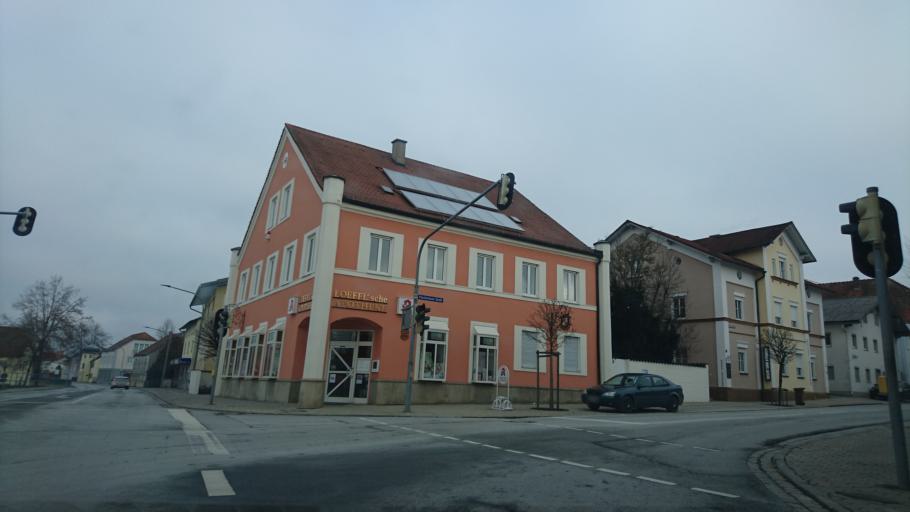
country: DE
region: Bavaria
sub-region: Lower Bavaria
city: Arnstorf
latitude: 48.5616
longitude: 12.8186
